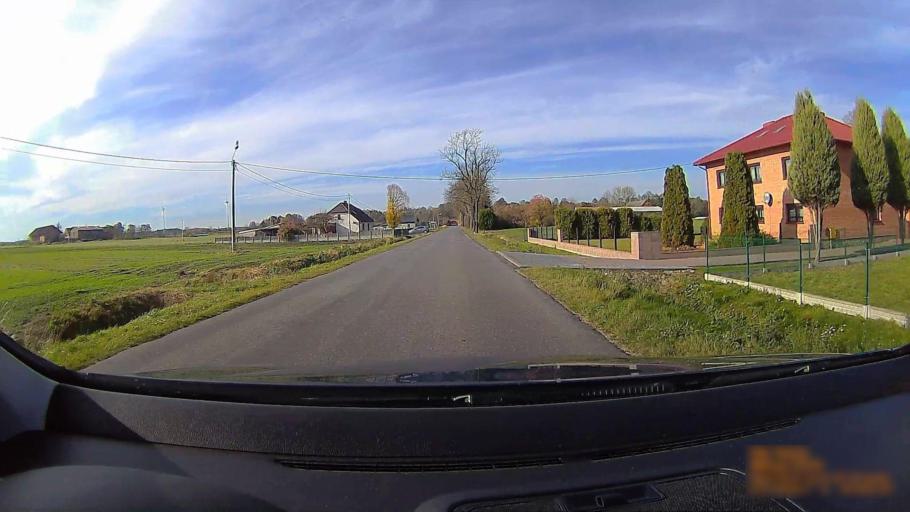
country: PL
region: Greater Poland Voivodeship
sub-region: Powiat ostrzeszowski
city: Doruchow
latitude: 51.4300
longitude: 18.0348
